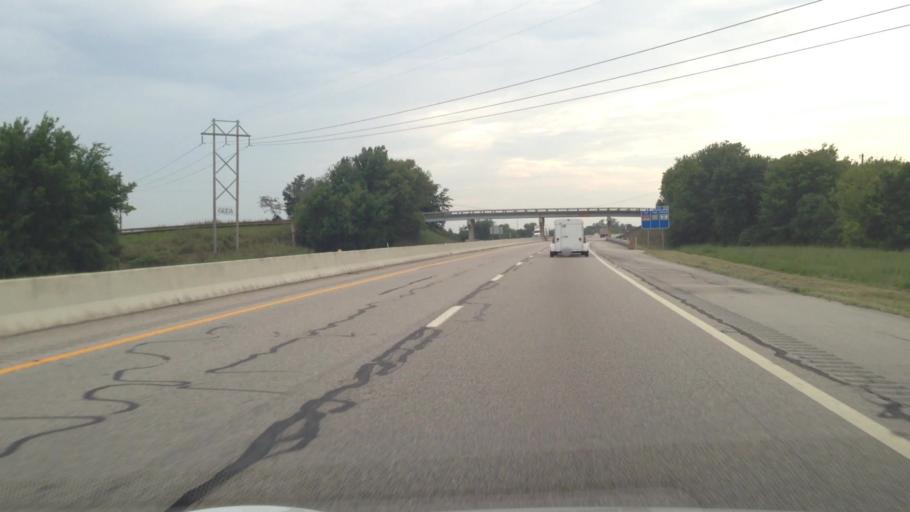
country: US
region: Oklahoma
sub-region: Ottawa County
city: Afton
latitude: 36.7297
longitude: -94.9184
